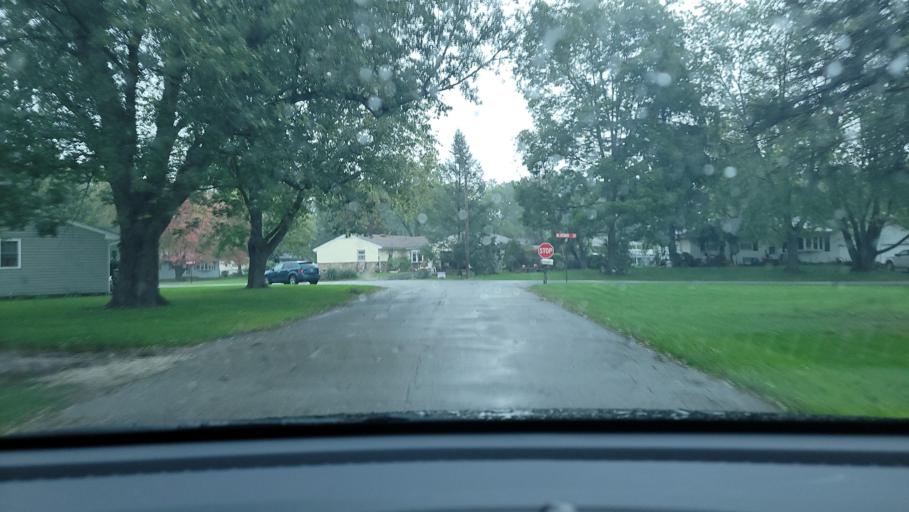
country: US
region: Indiana
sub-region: Porter County
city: Portage
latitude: 41.5912
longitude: -87.1804
